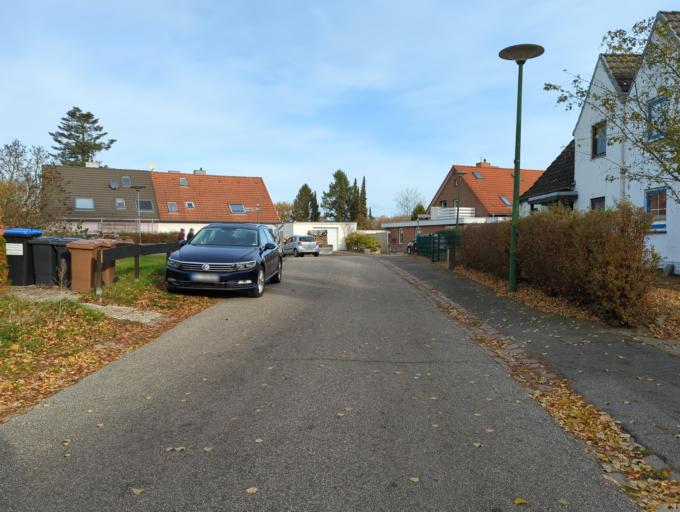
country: DE
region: Mecklenburg-Vorpommern
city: Selmsdorf
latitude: 53.8832
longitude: 10.8068
